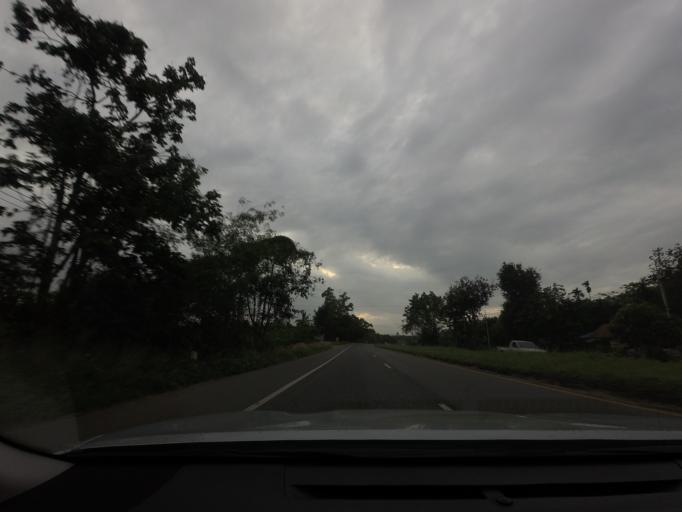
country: TH
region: Surat Thani
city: Phunphin
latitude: 9.0367
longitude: 99.1385
